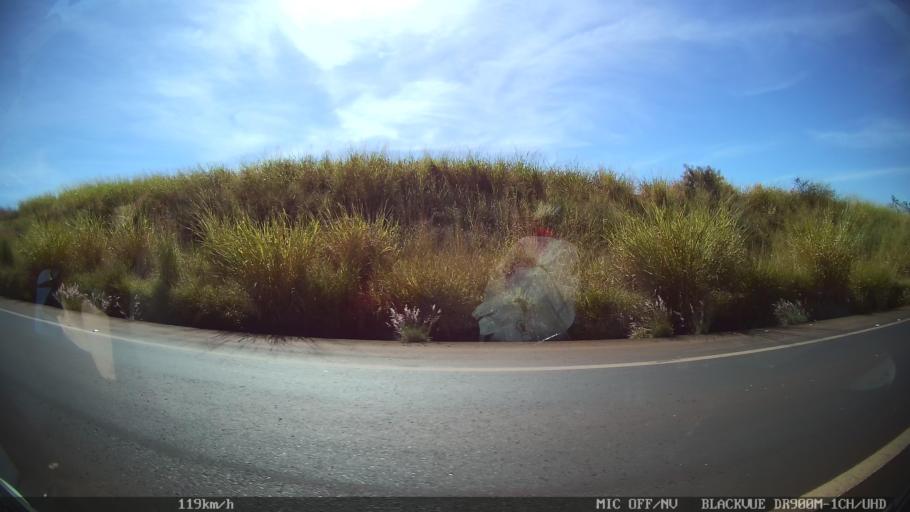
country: BR
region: Sao Paulo
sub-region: Sao Joaquim Da Barra
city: Sao Joaquim da Barra
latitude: -20.5607
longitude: -47.6909
